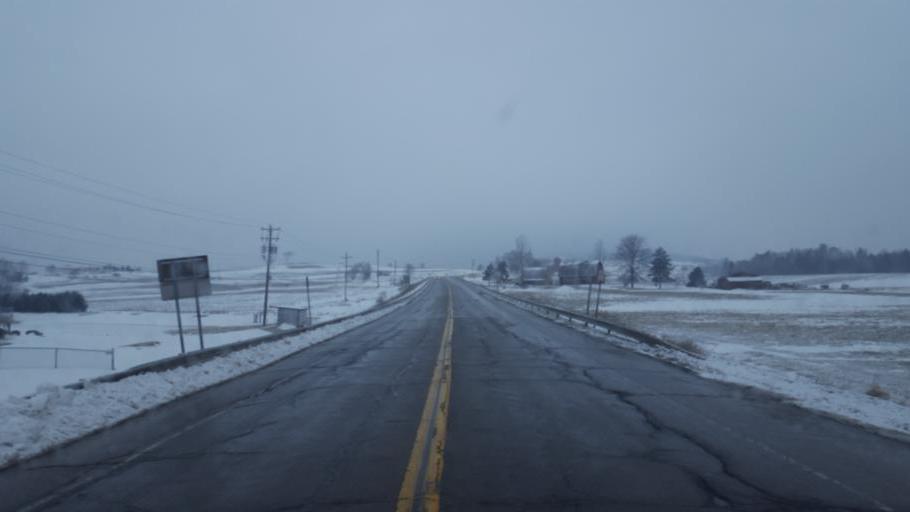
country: US
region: New York
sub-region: Steuben County
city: Canisteo
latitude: 42.1271
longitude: -77.5097
